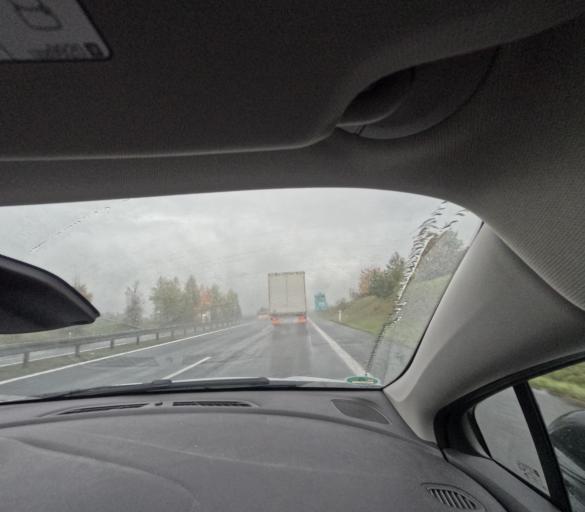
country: CZ
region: Central Bohemia
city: Velka Dobra
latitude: 50.1049
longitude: 14.0921
